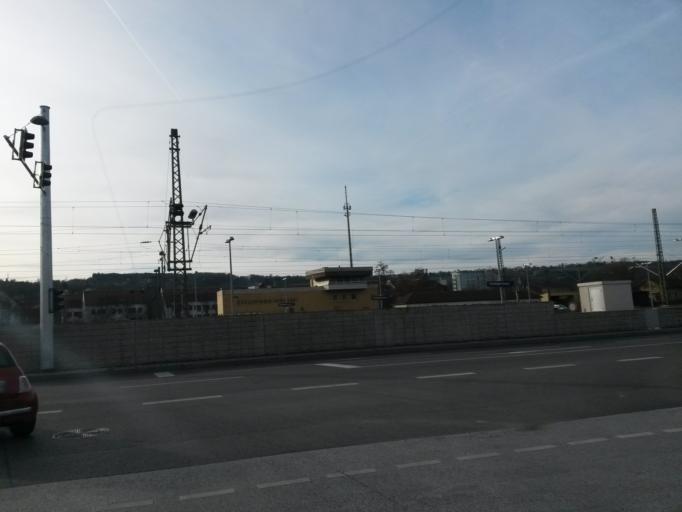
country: DE
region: Baden-Wuerttemberg
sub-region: Regierungsbezirk Stuttgart
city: Esslingen
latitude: 48.7394
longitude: 9.2997
